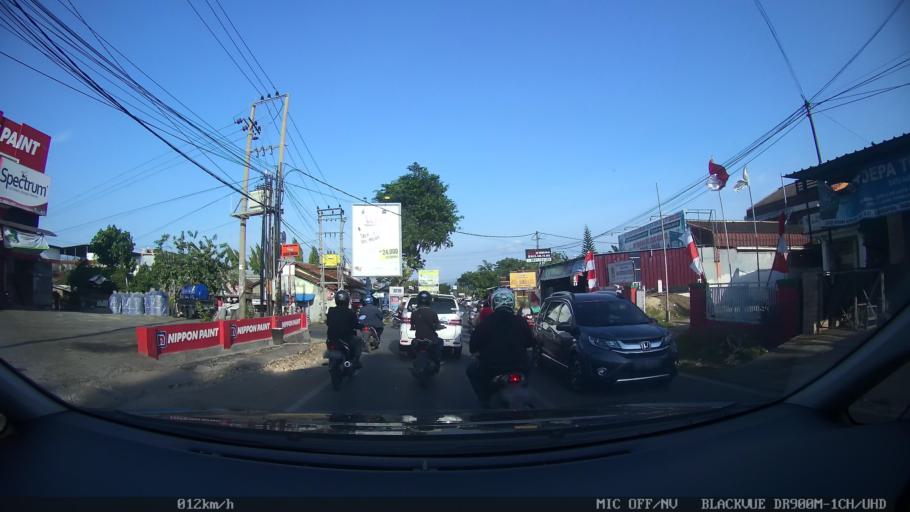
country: ID
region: Lampung
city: Kedaton
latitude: -5.3929
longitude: 105.2293
